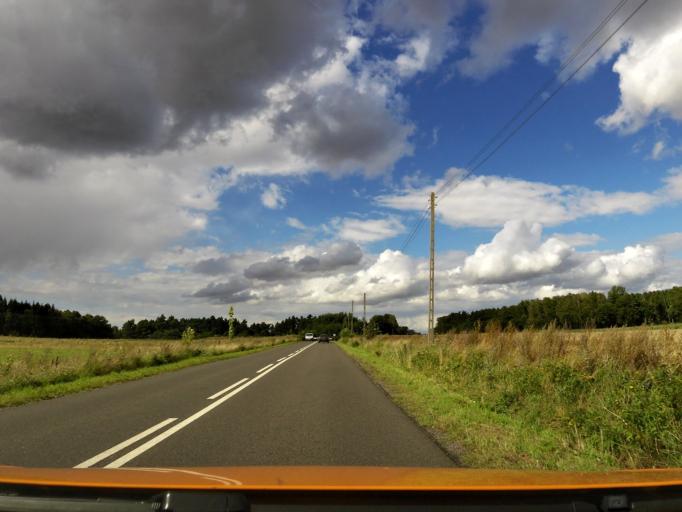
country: PL
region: West Pomeranian Voivodeship
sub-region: Powiat kolobrzeski
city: Ryman
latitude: 53.9766
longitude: 15.4893
